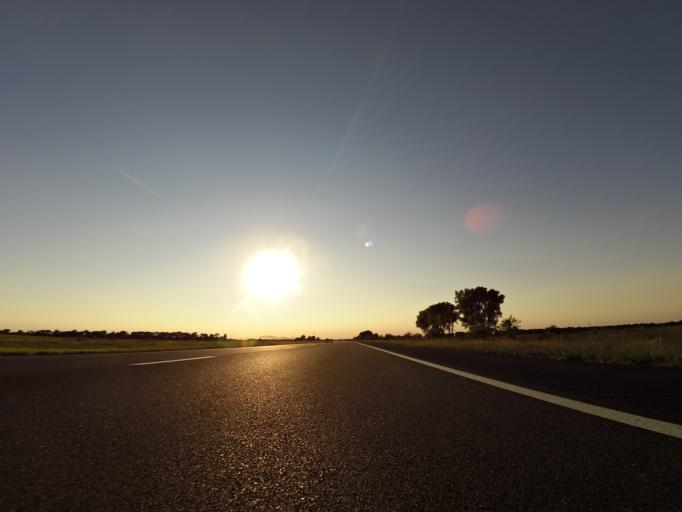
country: US
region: Kansas
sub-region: Reno County
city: Haven
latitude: 37.8873
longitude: -97.7398
